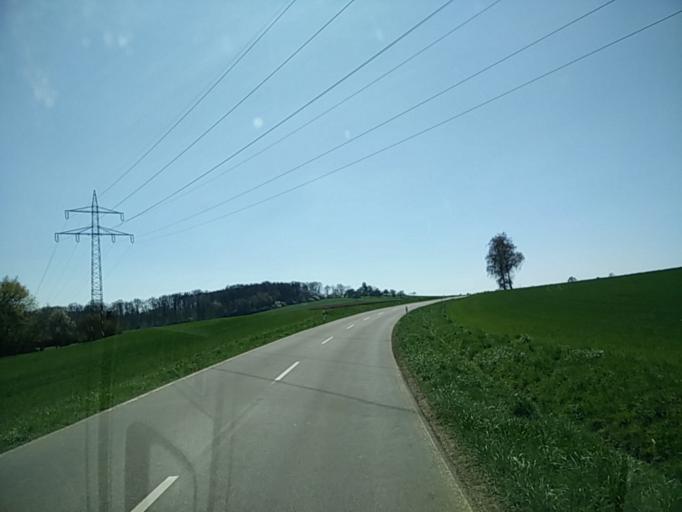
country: DE
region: Baden-Wuerttemberg
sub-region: Tuebingen Region
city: Dusslingen
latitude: 48.4602
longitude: 9.0713
